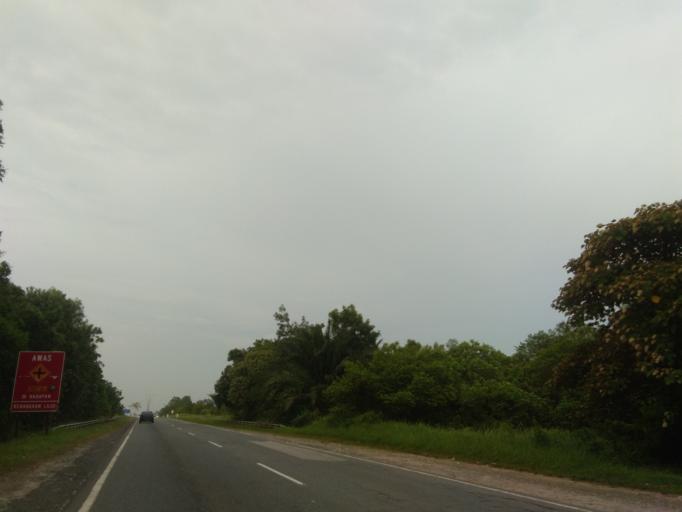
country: MY
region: Penang
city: Tasek Glugor
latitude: 5.5104
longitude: 100.6273
